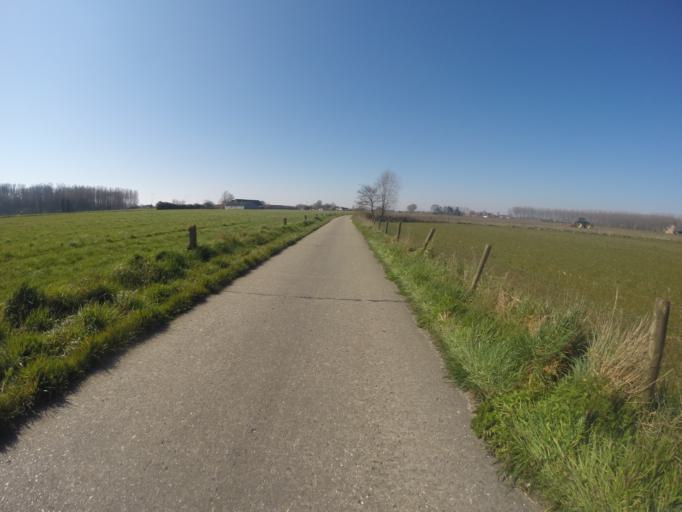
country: BE
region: Flanders
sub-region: Provincie Oost-Vlaanderen
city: Aalter
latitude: 51.0613
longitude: 3.4243
